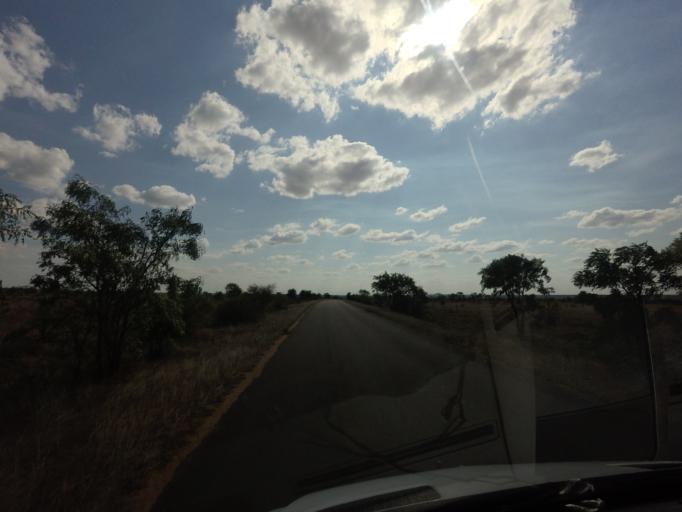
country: ZA
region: Limpopo
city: Thulamahashi
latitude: -24.3924
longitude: 31.6049
